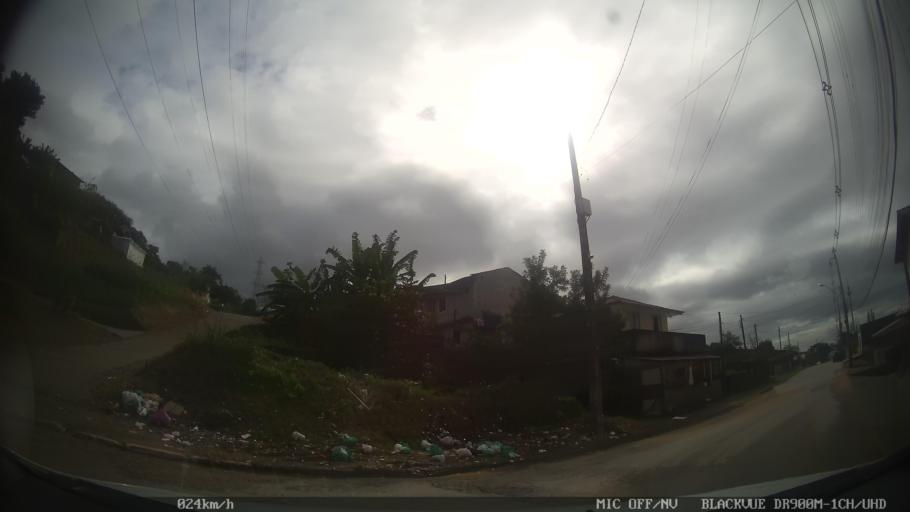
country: BR
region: Santa Catarina
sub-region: Biguacu
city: Biguacu
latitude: -27.5417
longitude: -48.6493
